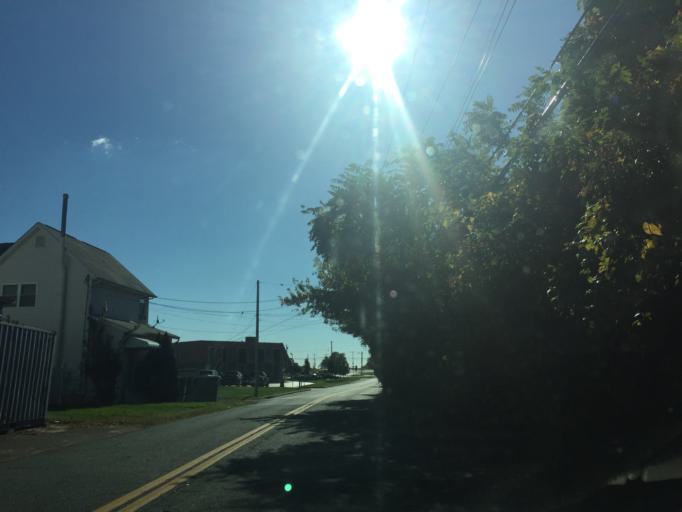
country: US
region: Maryland
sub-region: Baltimore County
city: Dundalk
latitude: 39.2665
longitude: -76.5188
